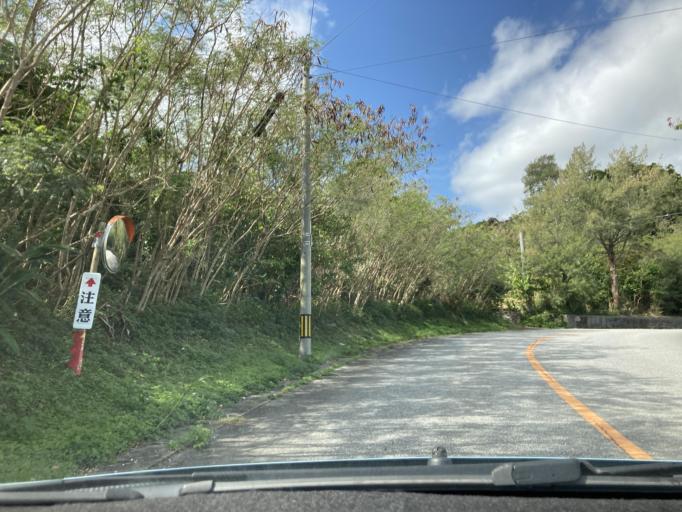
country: JP
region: Okinawa
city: Ginowan
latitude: 26.1800
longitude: 127.7665
